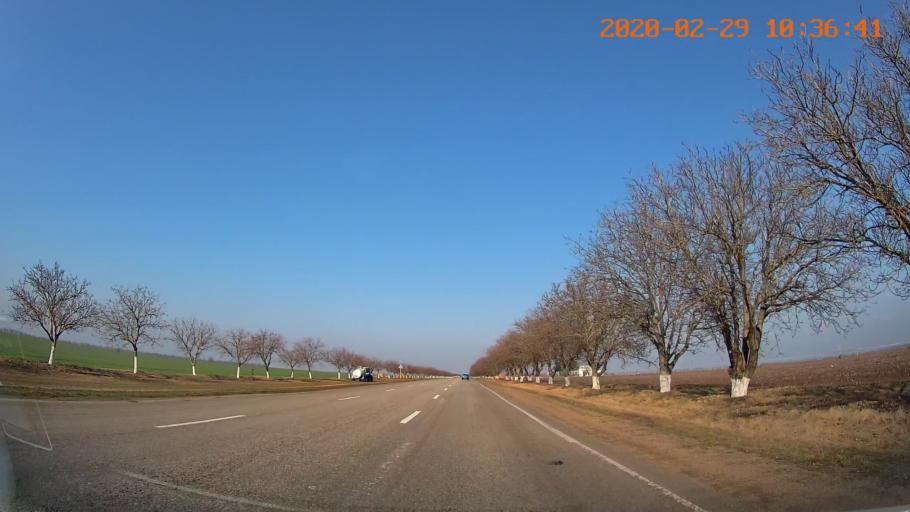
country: MD
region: Anenii Noi
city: Varnita
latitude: 46.9982
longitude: 29.5013
